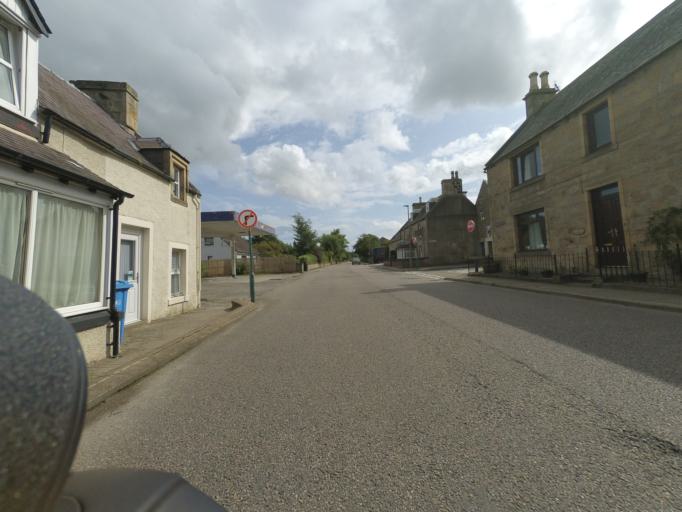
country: GB
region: Scotland
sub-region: Highland
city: Tain
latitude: 57.8092
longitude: -4.0517
